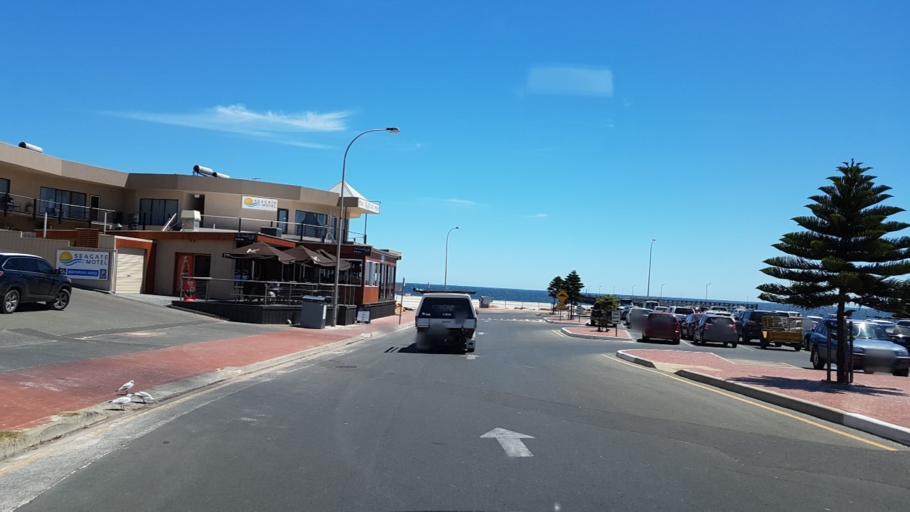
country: AU
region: South Australia
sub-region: Copper Coast
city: Wallaroo
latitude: -34.0549
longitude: 137.5621
